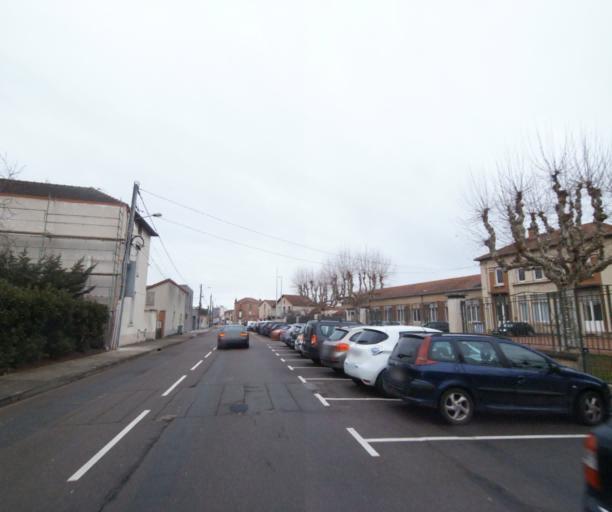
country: FR
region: Rhone-Alpes
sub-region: Departement de la Loire
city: Le Coteau
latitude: 46.0480
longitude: 4.0852
